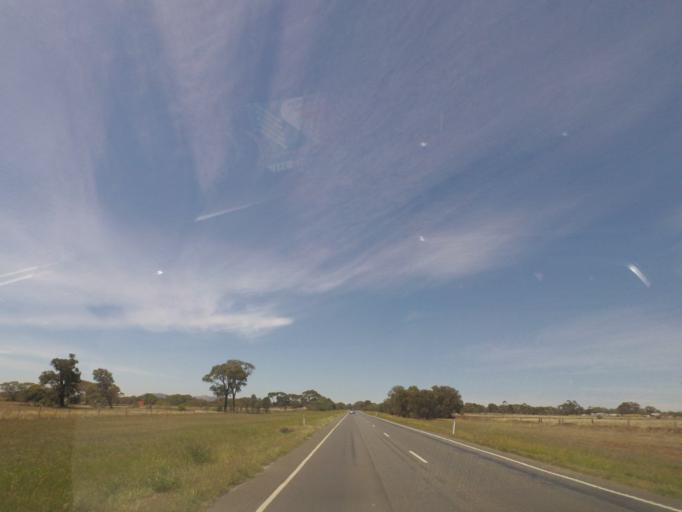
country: AU
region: Victoria
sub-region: Wyndham
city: Wyndham Vale
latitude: -37.8495
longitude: 144.3872
